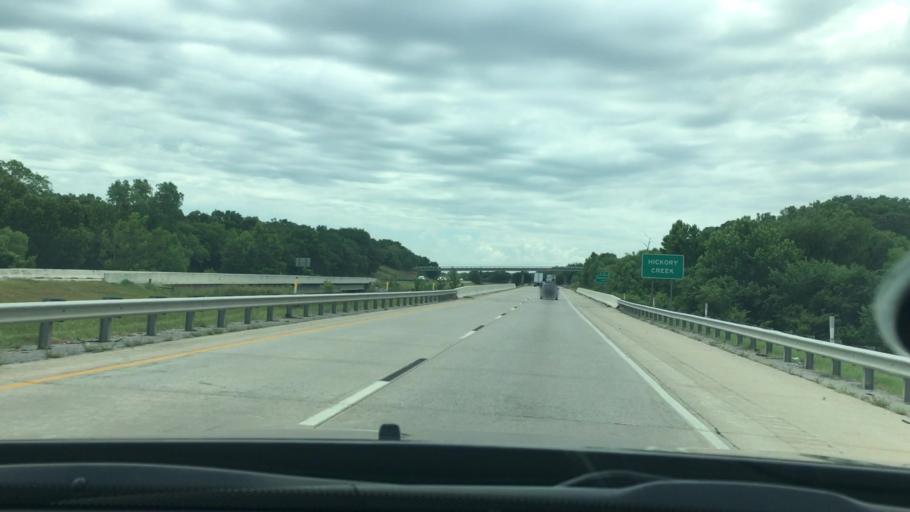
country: US
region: Oklahoma
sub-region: Love County
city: Marietta
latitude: 34.0458
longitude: -97.1497
